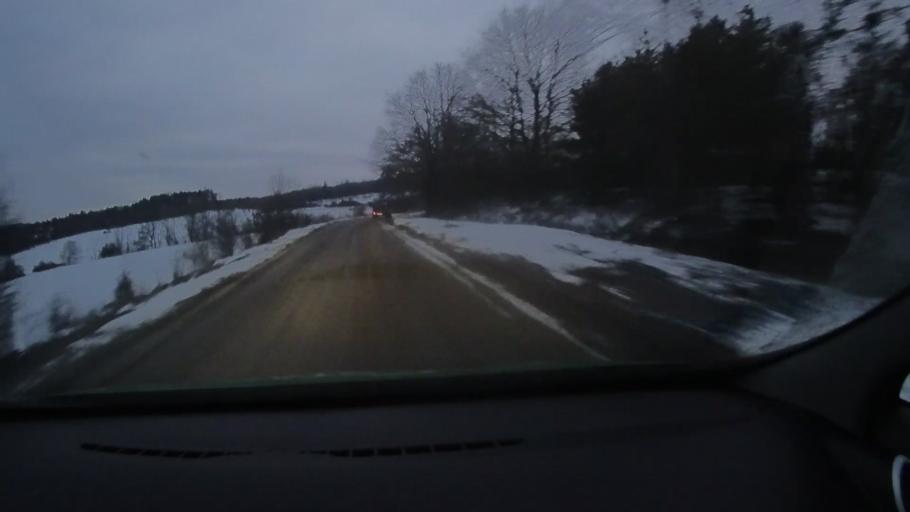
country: RO
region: Harghita
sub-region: Comuna Darjiu
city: Darjiu
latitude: 46.1877
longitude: 25.2475
